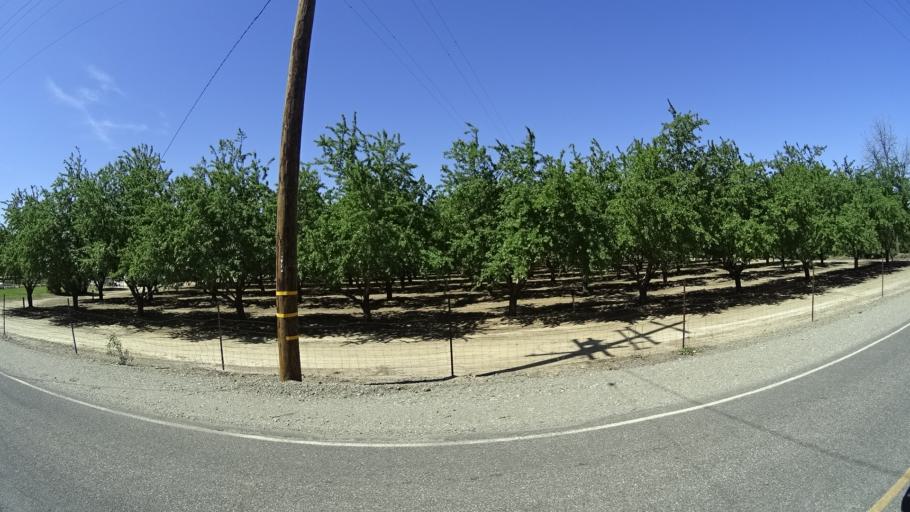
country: US
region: California
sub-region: Glenn County
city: Orland
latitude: 39.7179
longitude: -122.1784
